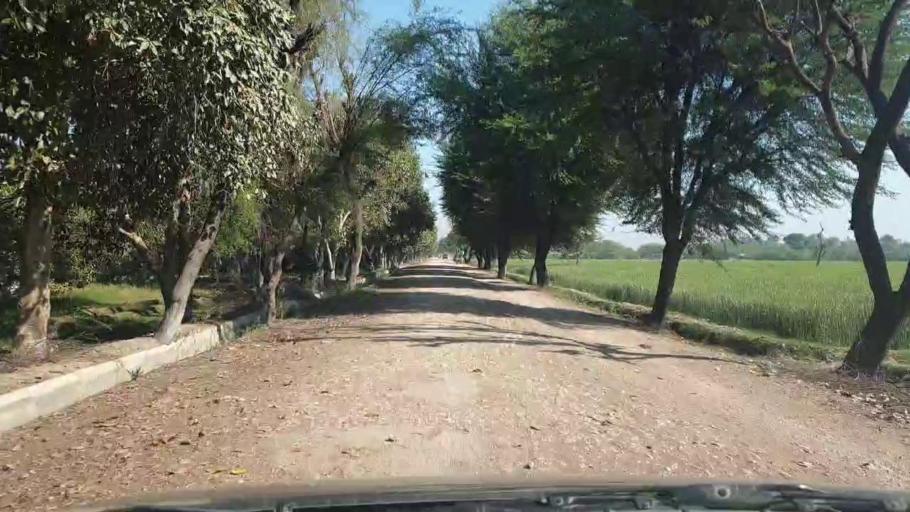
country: PK
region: Sindh
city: Umarkot
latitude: 25.3746
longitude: 69.7018
